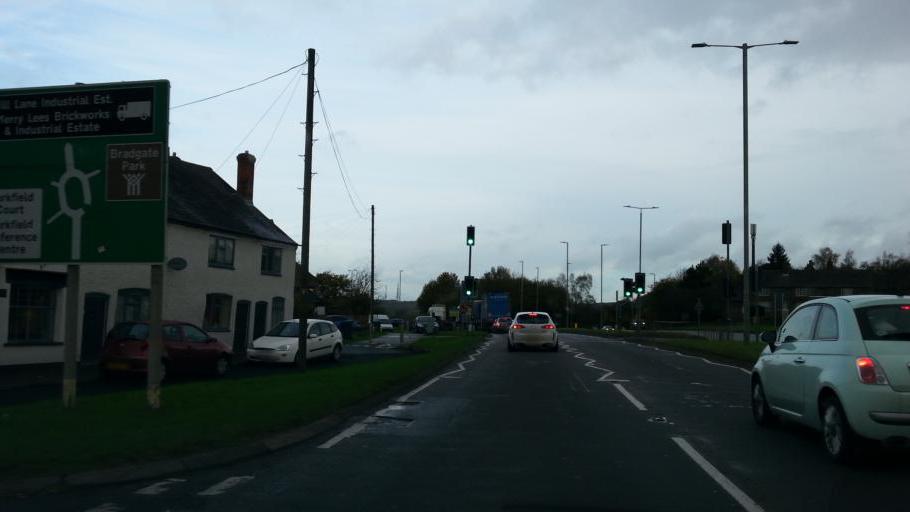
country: GB
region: England
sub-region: Leicestershire
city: Markfield
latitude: 52.6855
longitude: -1.2667
